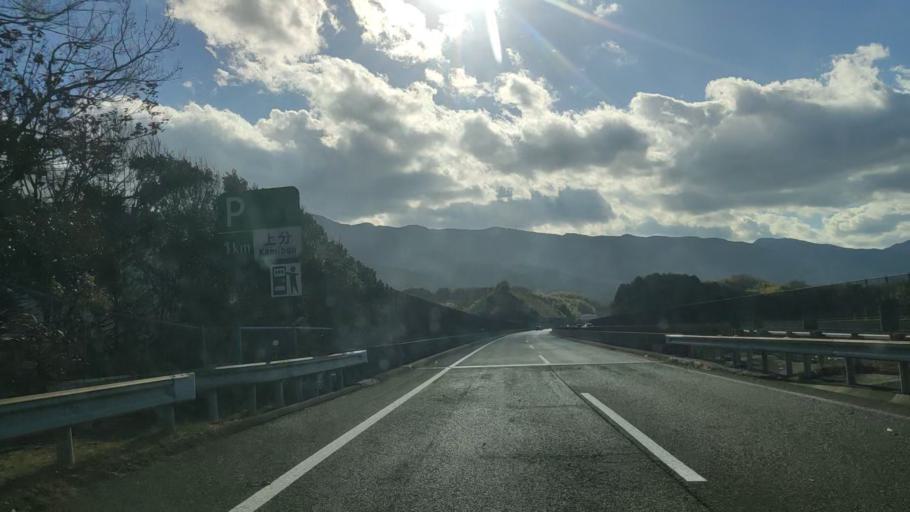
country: JP
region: Ehime
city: Kawanoecho
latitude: 33.9929
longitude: 133.5948
